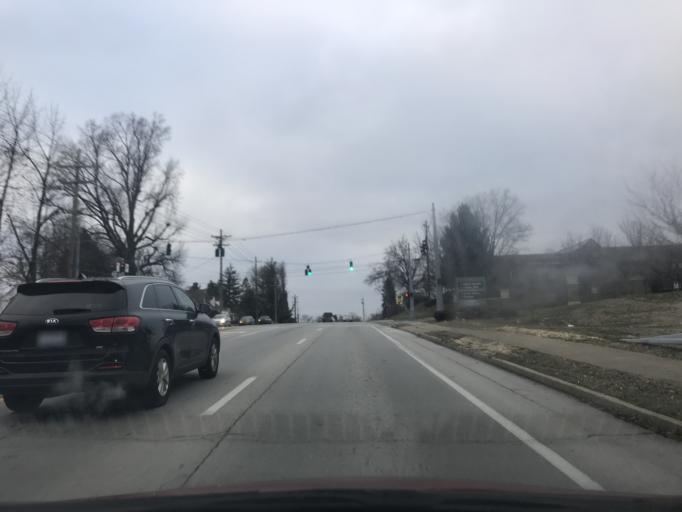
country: US
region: Kentucky
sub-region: Jefferson County
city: Audubon Park
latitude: 38.2173
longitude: -85.7262
